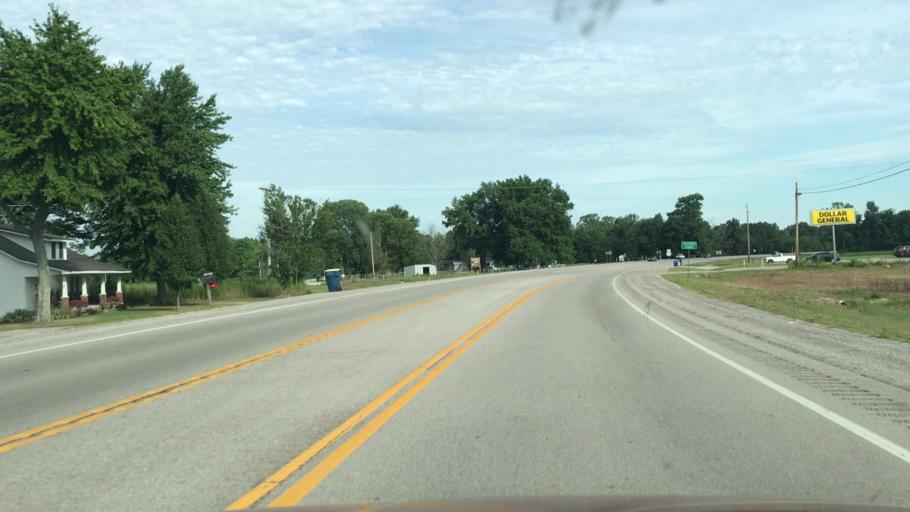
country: US
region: Kentucky
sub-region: Edmonson County
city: Brownsville
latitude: 37.1187
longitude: -86.2319
